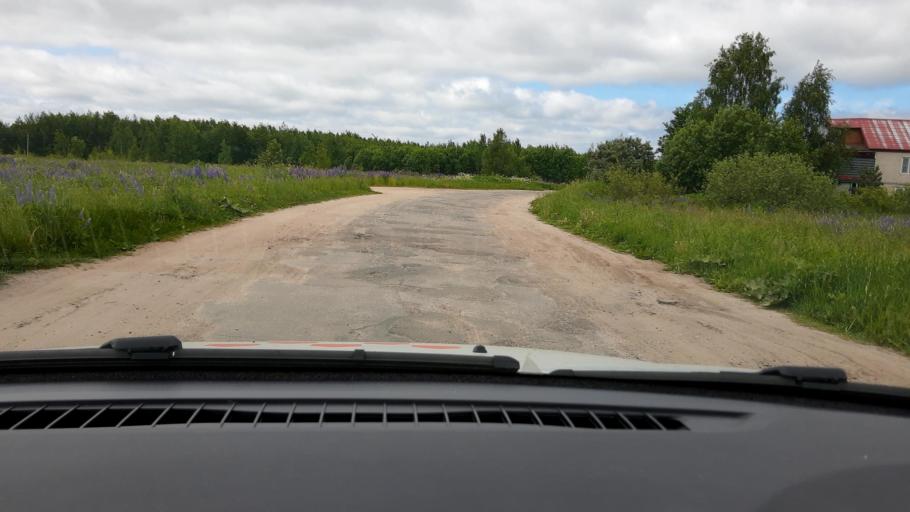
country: RU
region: Nizjnij Novgorod
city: Sitniki
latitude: 56.5192
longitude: 44.1078
